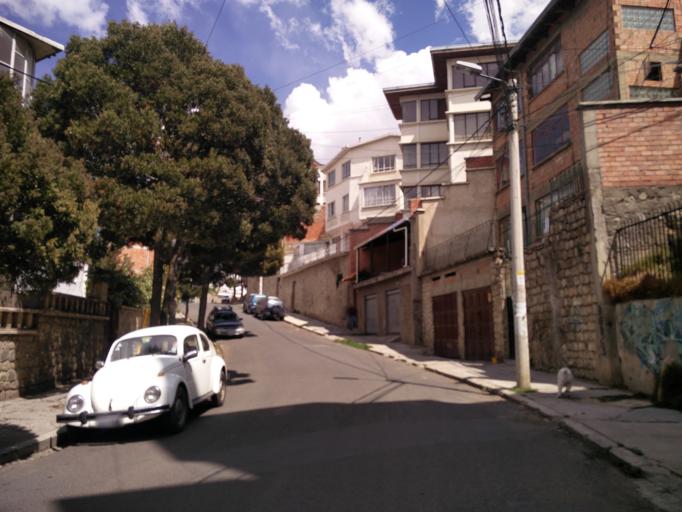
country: BO
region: La Paz
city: La Paz
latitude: -16.5097
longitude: -68.1336
